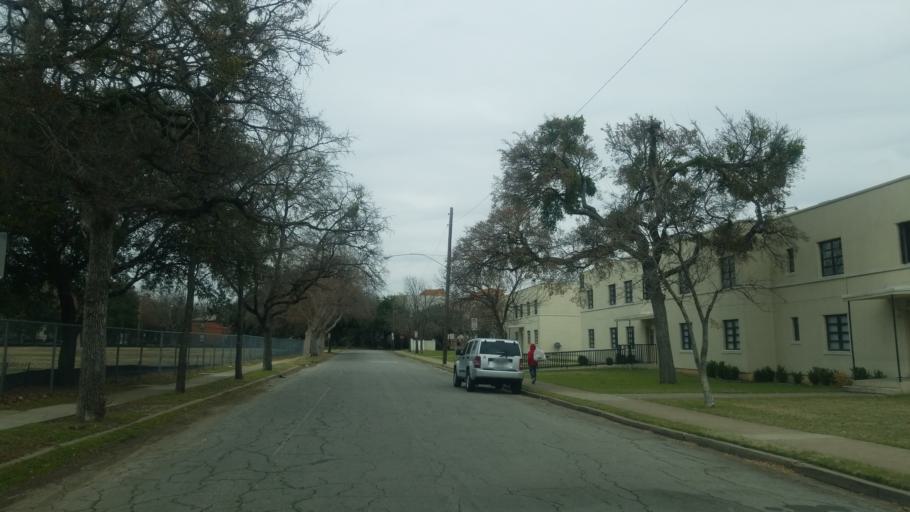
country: US
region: Texas
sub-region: Dallas County
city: Highland Park
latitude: 32.8148
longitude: -96.8215
